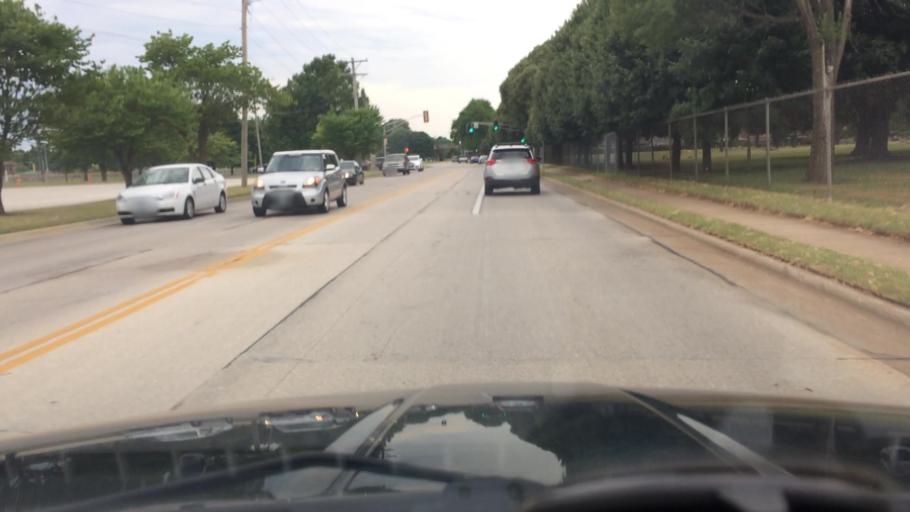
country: US
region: Missouri
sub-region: Greene County
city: Springfield
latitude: 37.1670
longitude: -93.2644
